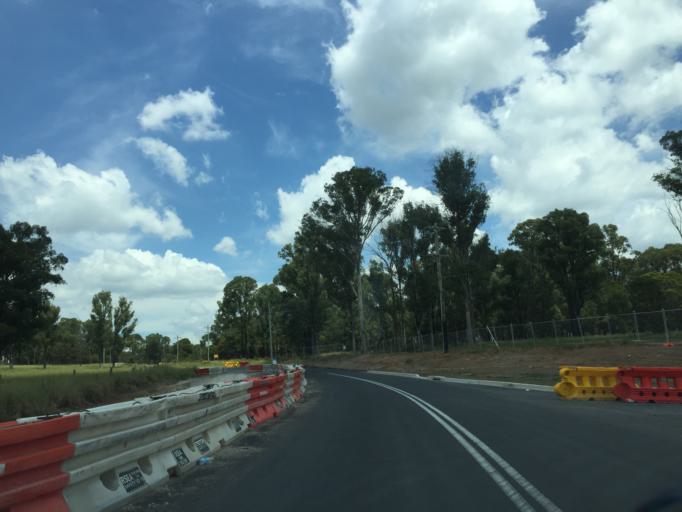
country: AU
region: New South Wales
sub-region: Blacktown
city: Hassall Grove
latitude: -33.7194
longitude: 150.8362
